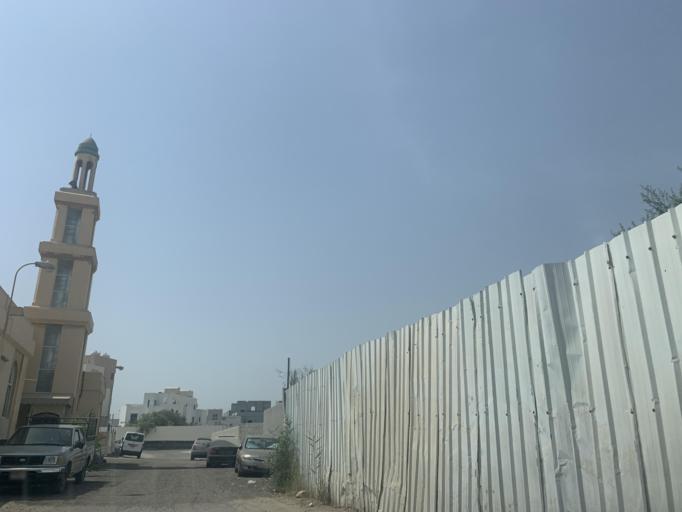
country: BH
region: Northern
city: Madinat `Isa
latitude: 26.1927
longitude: 50.4904
